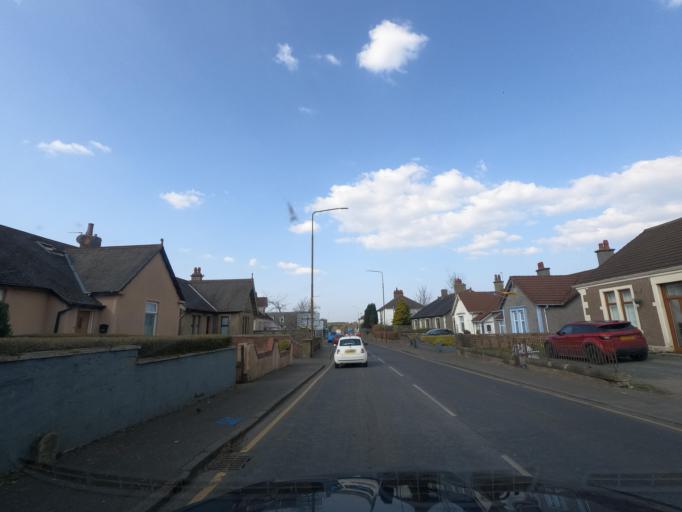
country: GB
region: Scotland
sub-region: West Lothian
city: Whitburn
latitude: 55.8656
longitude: -3.6844
